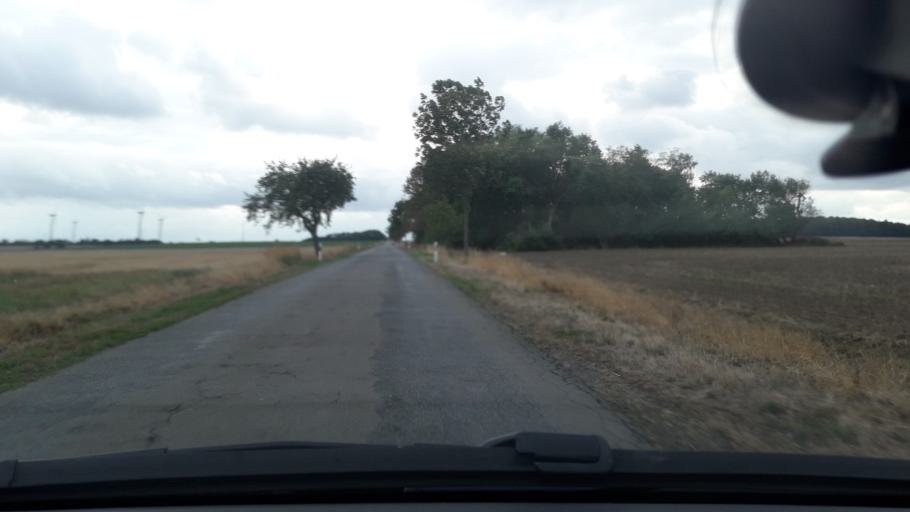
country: DE
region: Lower Saxony
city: Velpke
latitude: 52.3905
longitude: 10.9600
